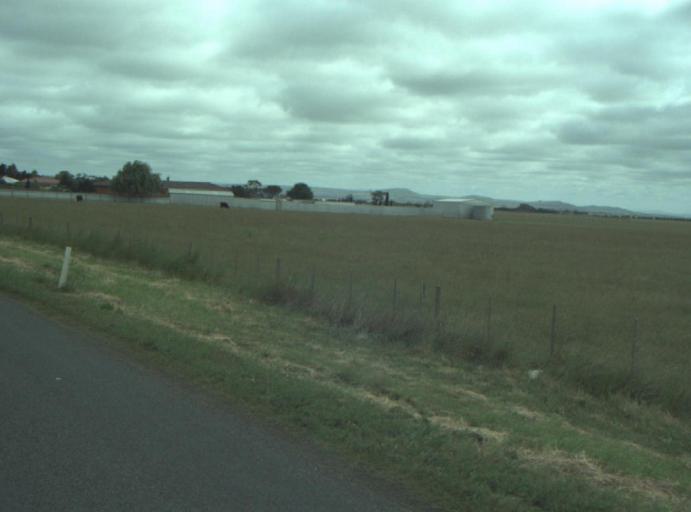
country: AU
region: Victoria
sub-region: Greater Geelong
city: Bell Post Hill
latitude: -38.0321
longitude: 144.2963
